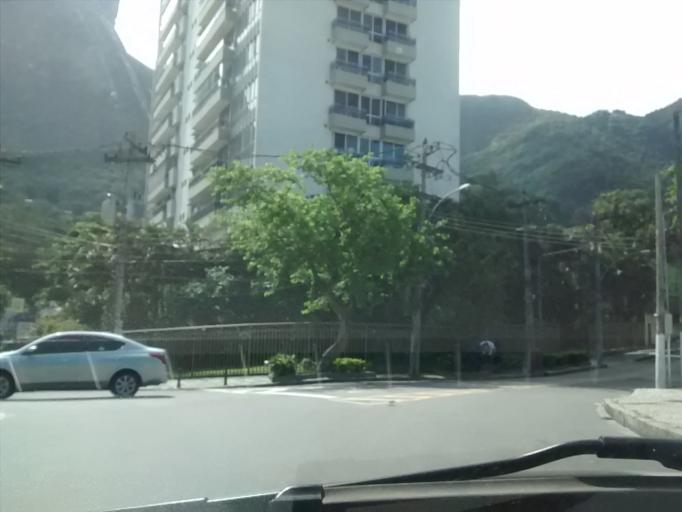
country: BR
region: Rio de Janeiro
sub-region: Rio De Janeiro
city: Rio de Janeiro
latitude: -22.9986
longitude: -43.2693
